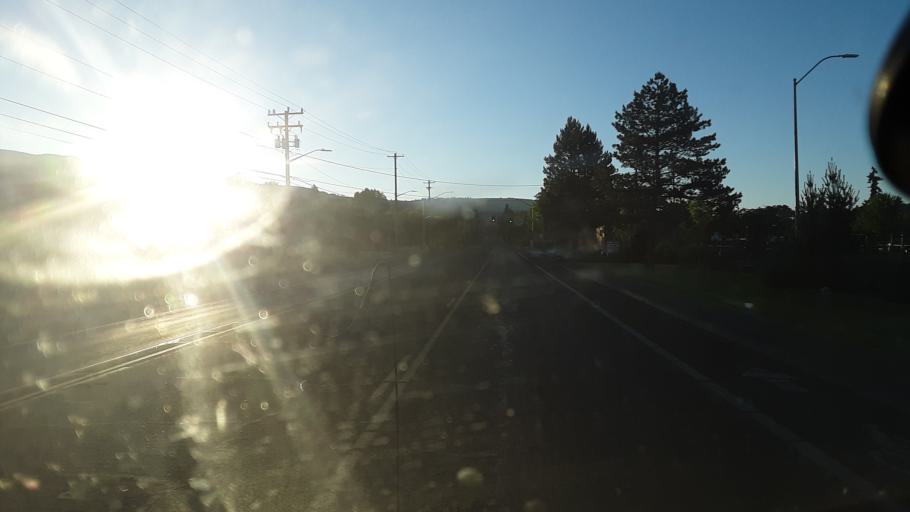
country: US
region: Oregon
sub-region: Klamath County
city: Altamont
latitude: 42.2138
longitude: -121.7540
